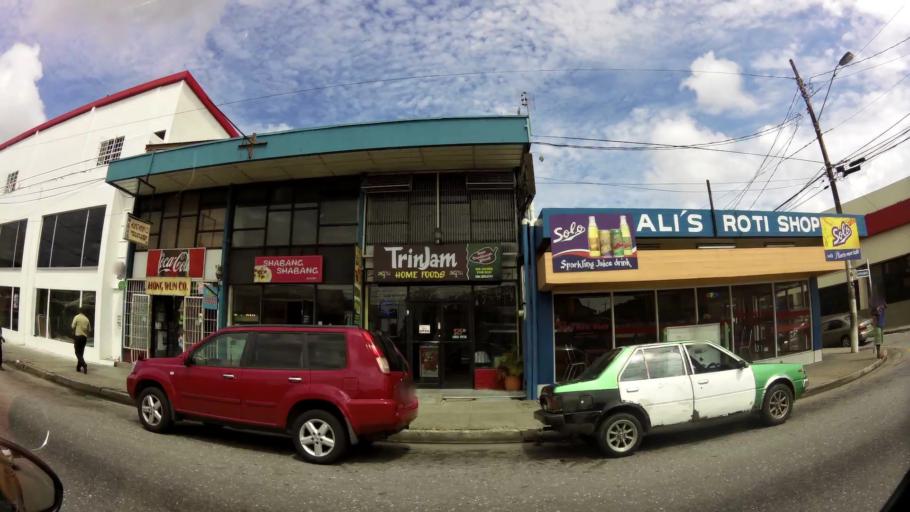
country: TT
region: City of Port of Spain
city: Mucurapo
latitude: 10.6710
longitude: -61.5303
